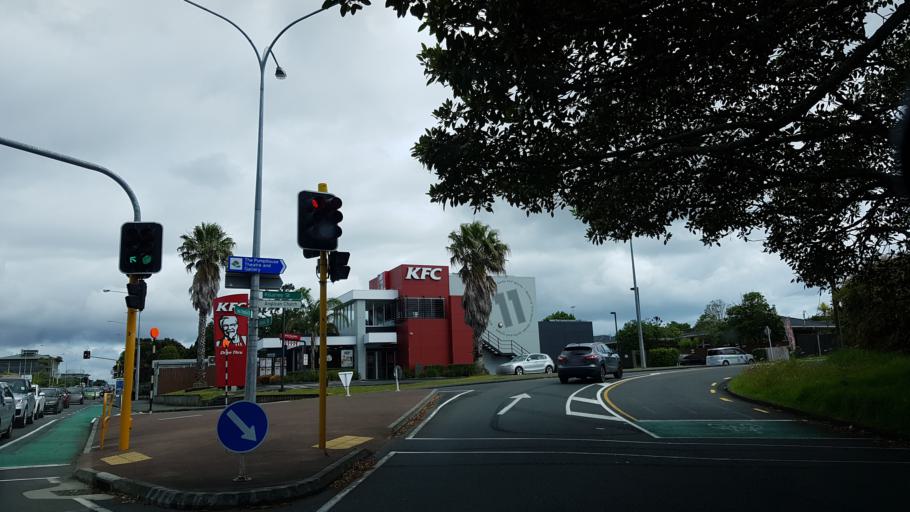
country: NZ
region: Auckland
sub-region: Auckland
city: North Shore
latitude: -36.7900
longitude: 174.7621
